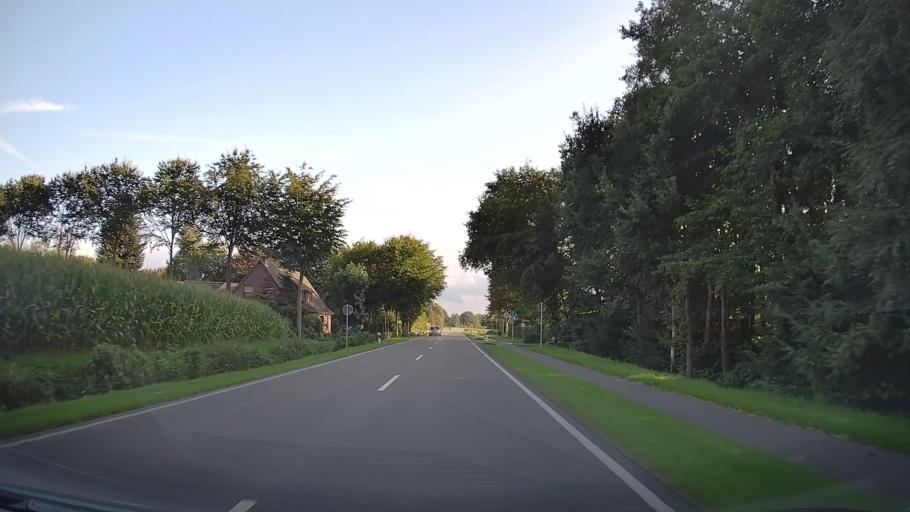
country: DE
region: Lower Saxony
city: Barssel
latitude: 53.0840
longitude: 7.7168
